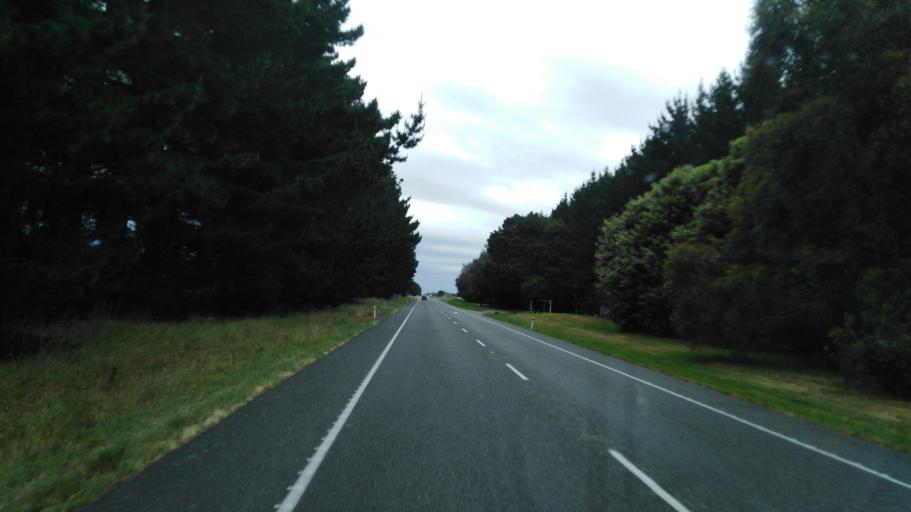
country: NZ
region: Manawatu-Wanganui
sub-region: Horowhenua District
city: Foxton
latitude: -40.4174
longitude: 175.3062
